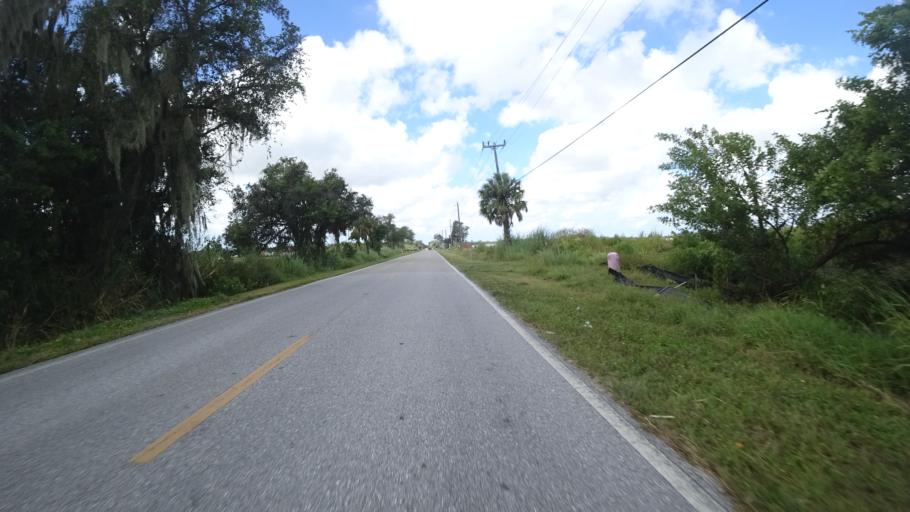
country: US
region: Florida
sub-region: Manatee County
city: Samoset
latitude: 27.4768
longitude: -82.5120
